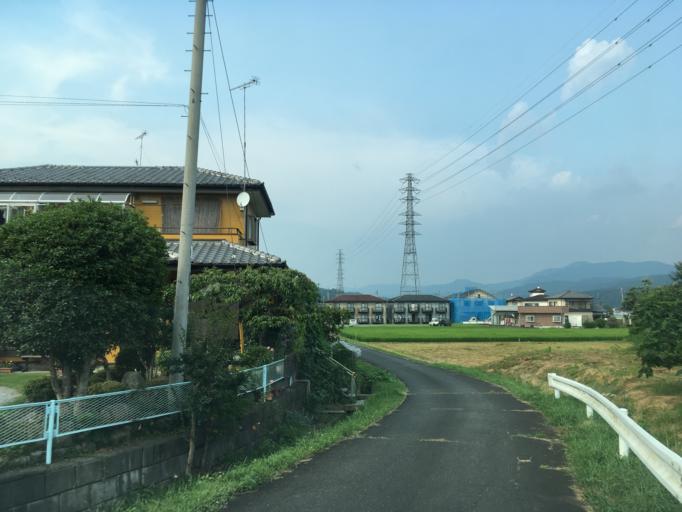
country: JP
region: Saitama
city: Chichibu
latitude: 35.9928
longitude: 139.0946
